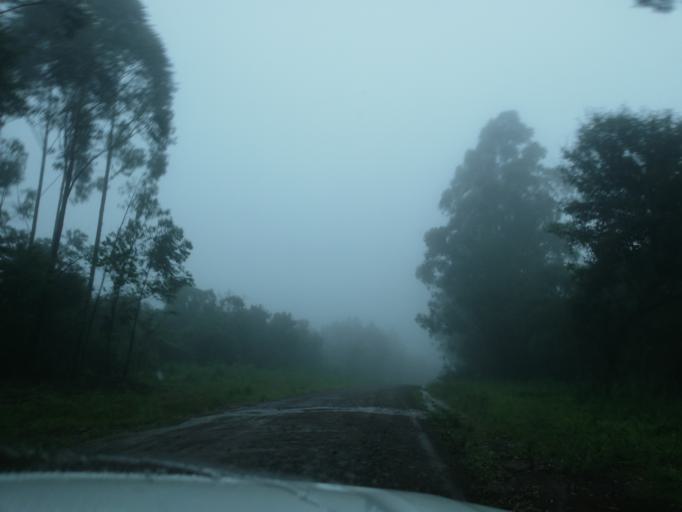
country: AR
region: Misiones
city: Almafuerte
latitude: -27.5322
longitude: -55.4062
